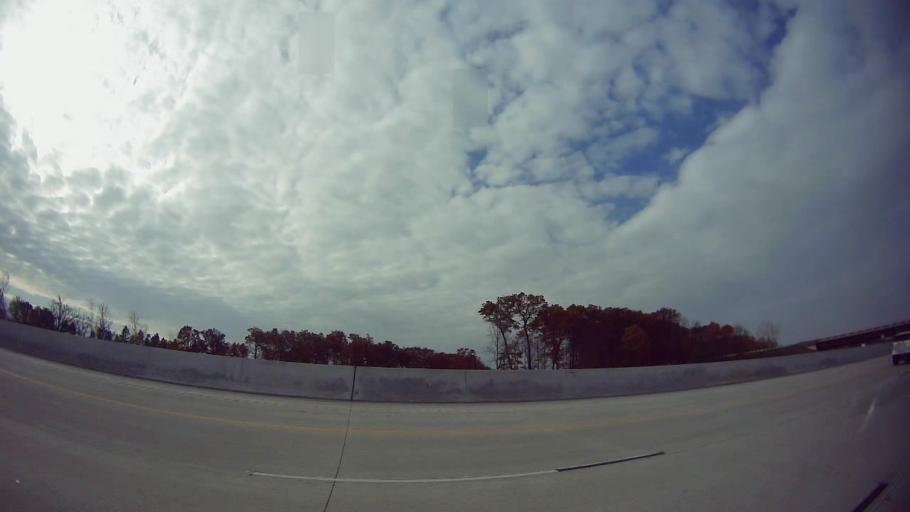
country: US
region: Michigan
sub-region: Oakland County
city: Bloomfield Hills
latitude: 42.6120
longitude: -83.2284
